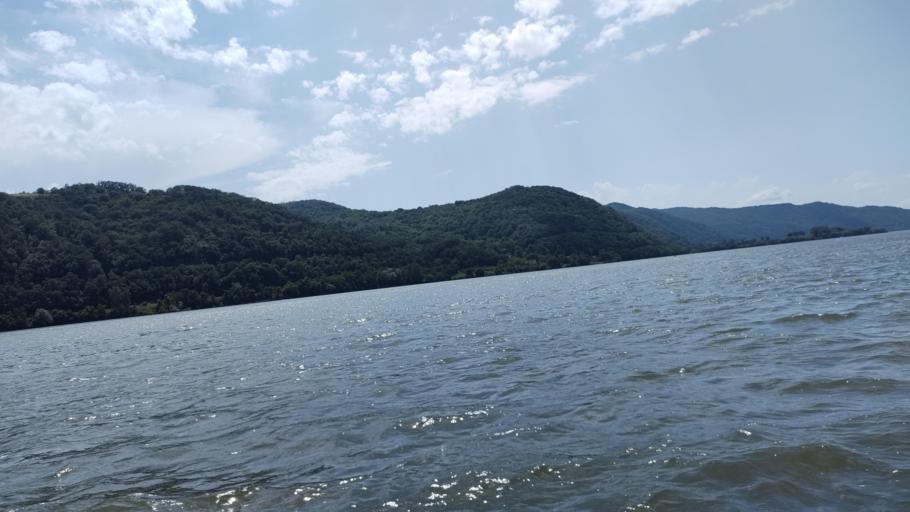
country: RO
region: Caras-Severin
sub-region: Comuna Berzasca
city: Liubcova
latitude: 44.6510
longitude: 21.8666
